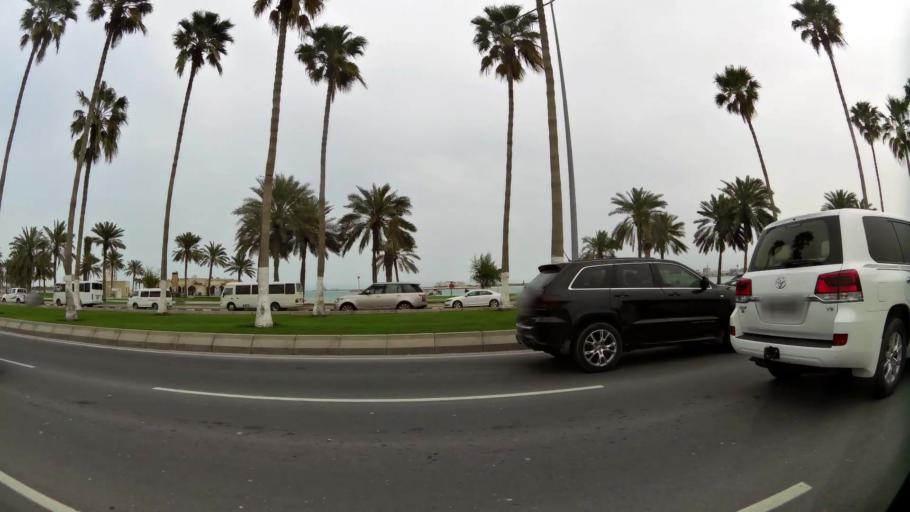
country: QA
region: Baladiyat ad Dawhah
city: Doha
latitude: 25.3069
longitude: 51.5179
